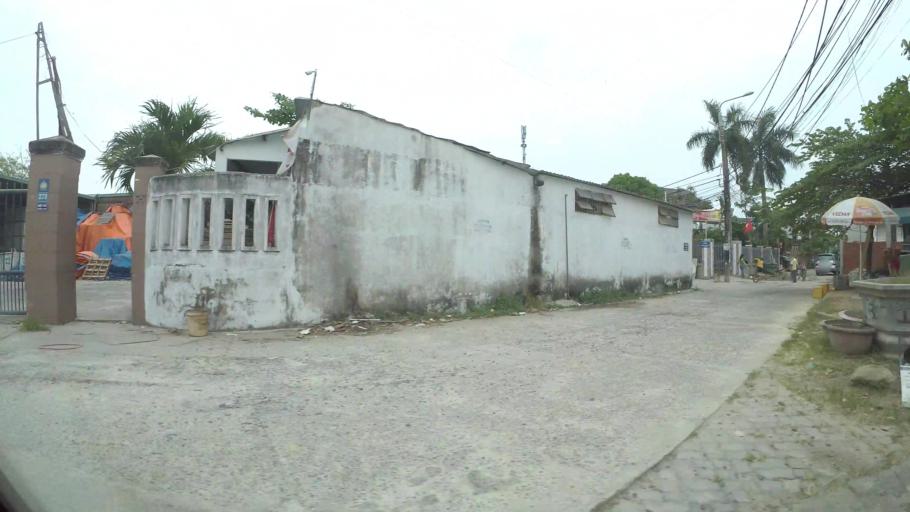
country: VN
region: Da Nang
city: Thanh Khe
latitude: 16.0476
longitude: 108.1764
